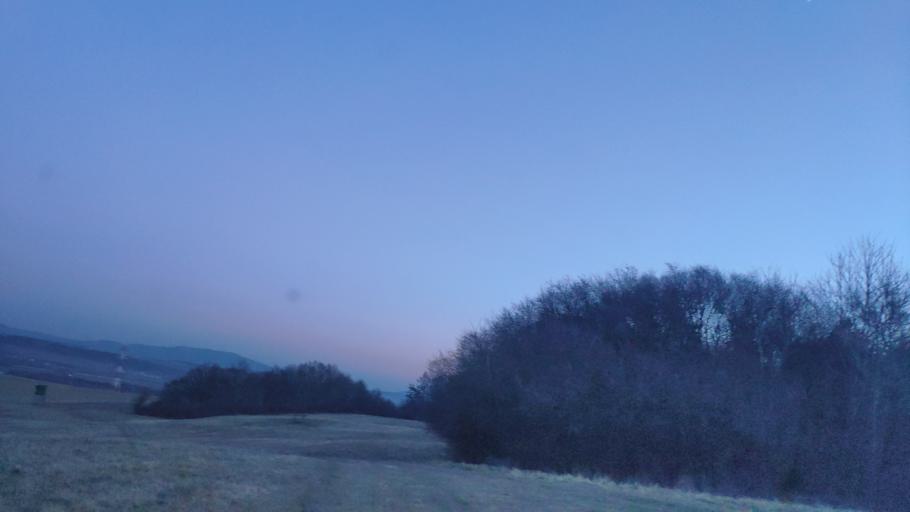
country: SK
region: Kosicky
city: Kosice
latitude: 48.8331
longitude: 21.2573
